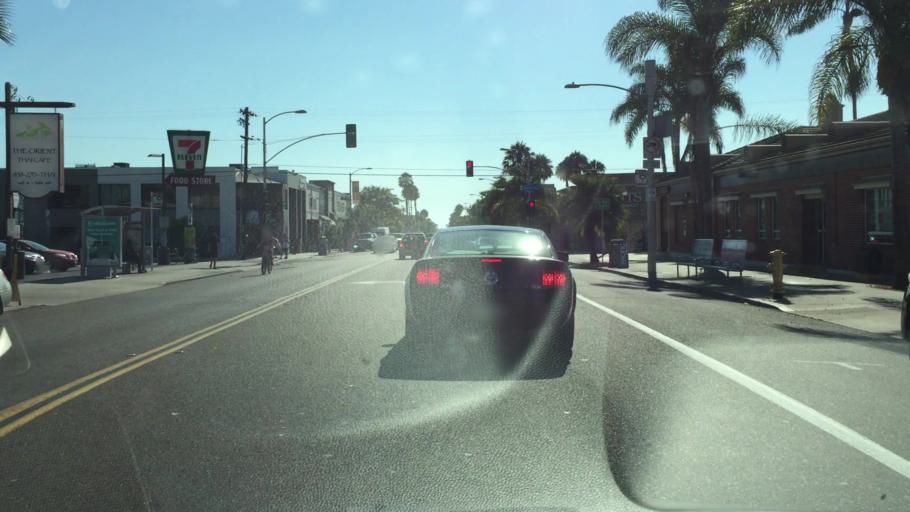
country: US
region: California
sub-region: San Diego County
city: La Jolla
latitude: 32.7988
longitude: -117.2457
